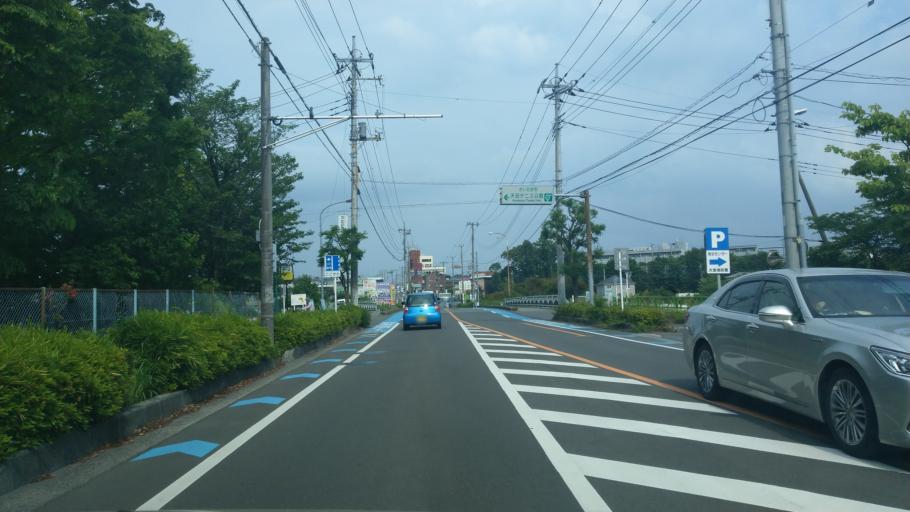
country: JP
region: Saitama
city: Saitama
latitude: 35.9080
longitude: 139.6477
